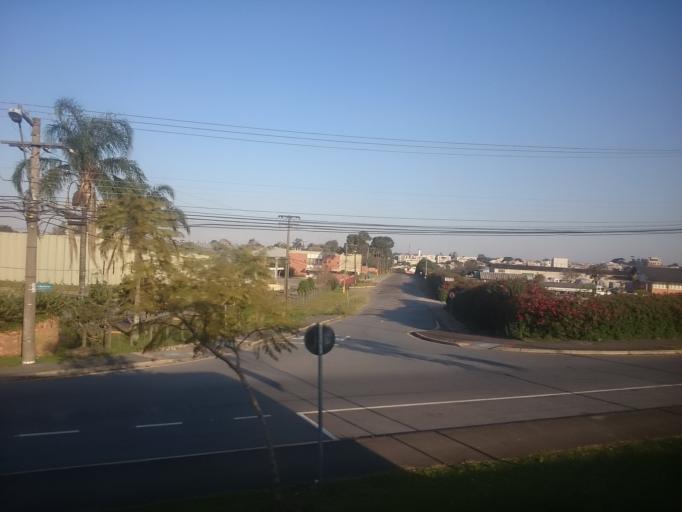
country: BR
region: Parana
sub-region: Curitiba
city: Curitiba
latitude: -25.4874
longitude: -49.2684
